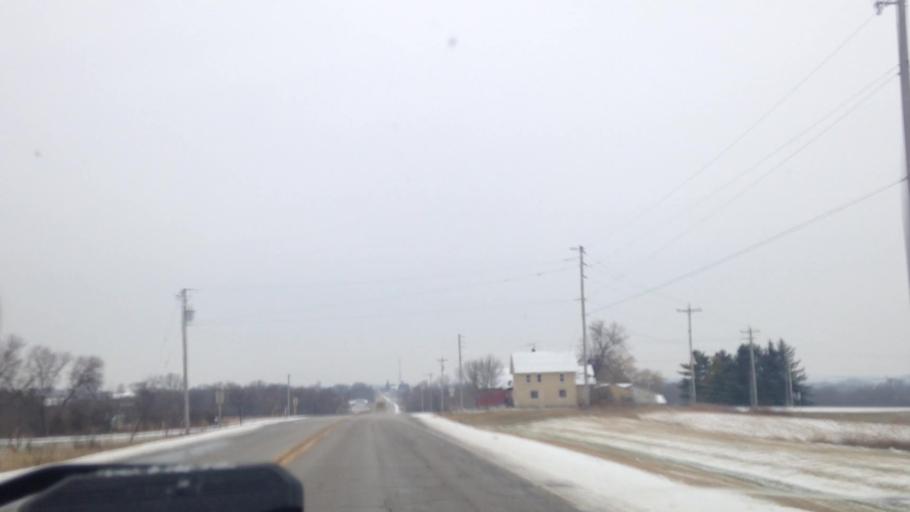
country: US
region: Wisconsin
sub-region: Dodge County
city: Mayville
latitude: 43.4153
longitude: -88.5421
